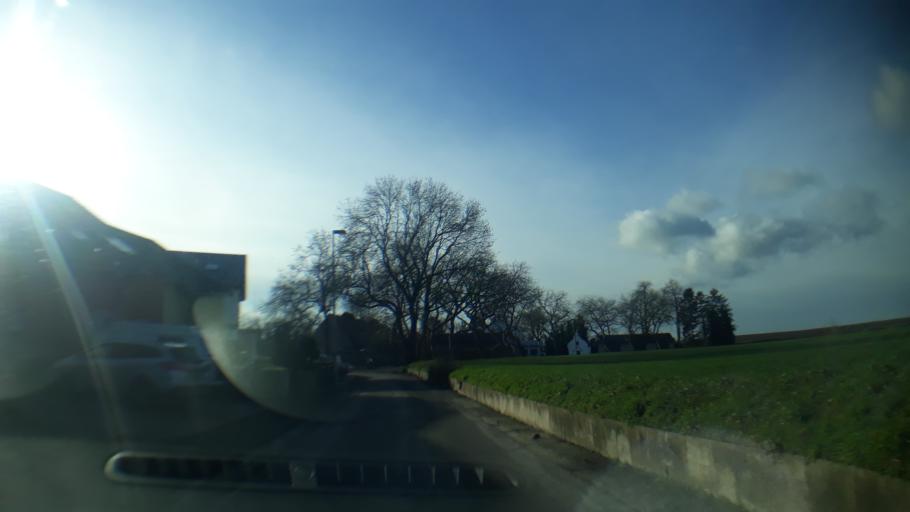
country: DE
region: North Rhine-Westphalia
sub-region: Regierungsbezirk Koln
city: Bedburg
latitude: 50.9892
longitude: 6.5487
